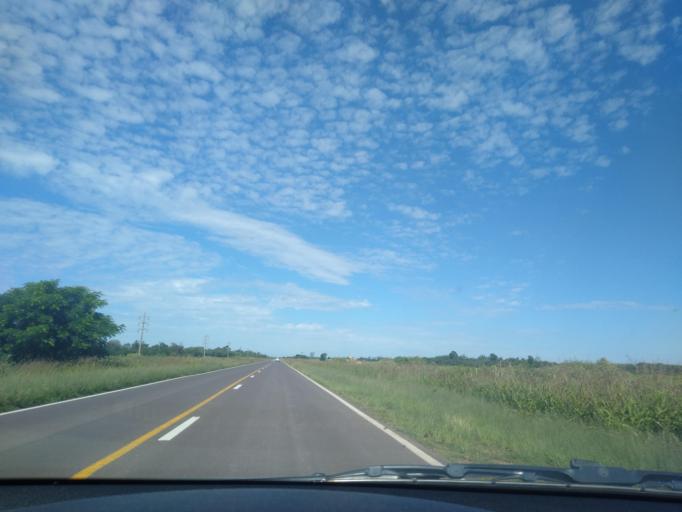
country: AR
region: Chaco
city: Presidencia Roque Saenz Pena
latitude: -26.7452
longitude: -60.3888
